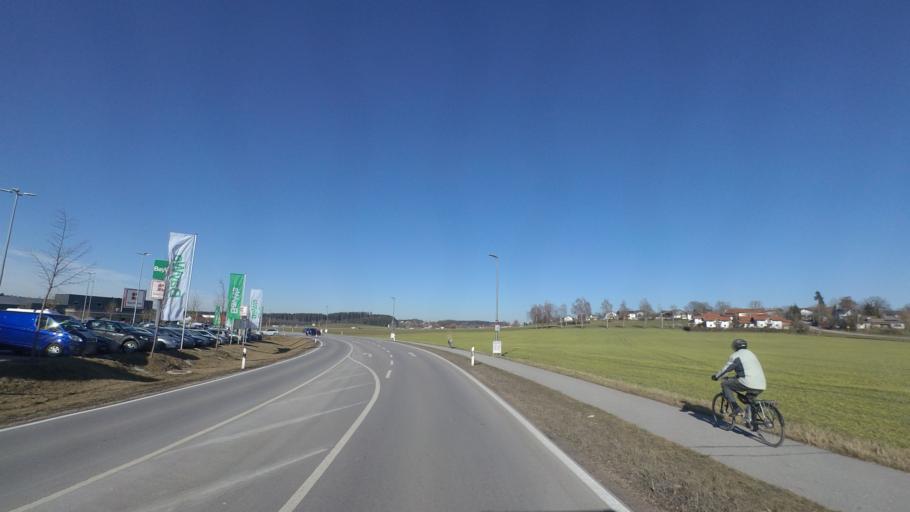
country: DE
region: Bavaria
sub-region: Upper Bavaria
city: Traunreut
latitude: 47.9649
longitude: 12.6118
